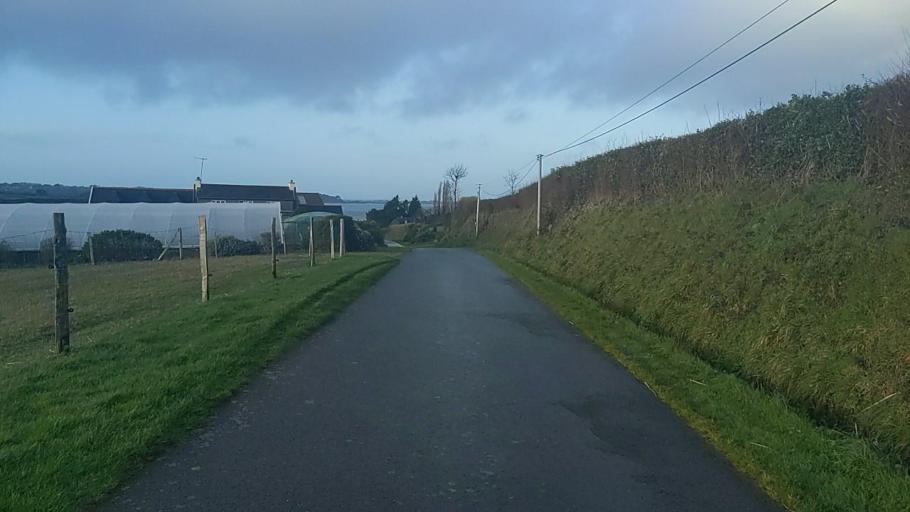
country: FR
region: Brittany
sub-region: Departement des Cotes-d'Armor
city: Plougrescant
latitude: 48.8235
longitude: -3.1966
